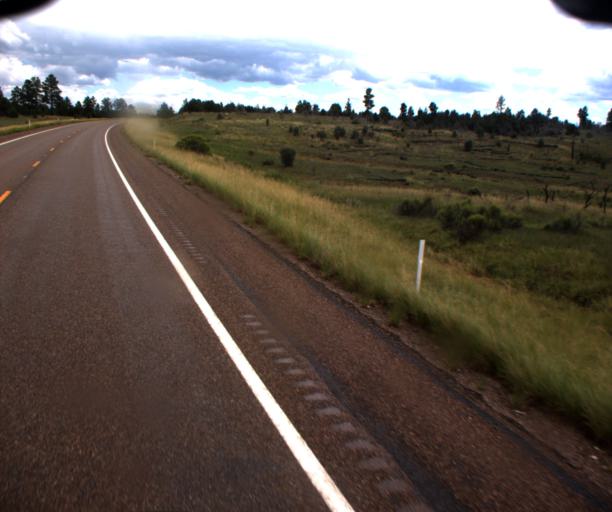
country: US
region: Arizona
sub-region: Navajo County
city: Linden
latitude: 34.3632
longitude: -110.3285
